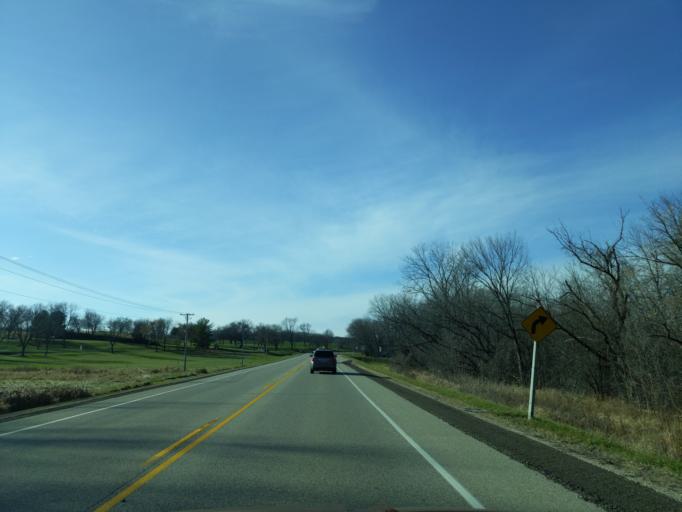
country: US
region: Wisconsin
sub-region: Rock County
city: Edgerton
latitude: 42.8271
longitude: -89.0129
